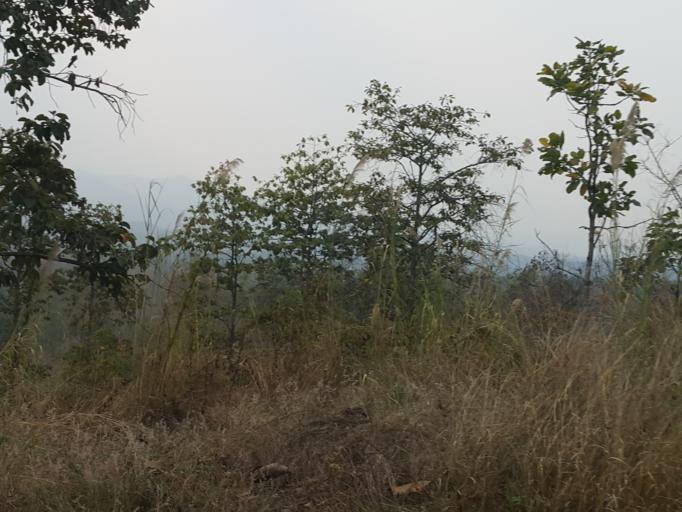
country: TH
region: Chiang Mai
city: Mae Taeng
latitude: 18.9685
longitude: 98.9294
